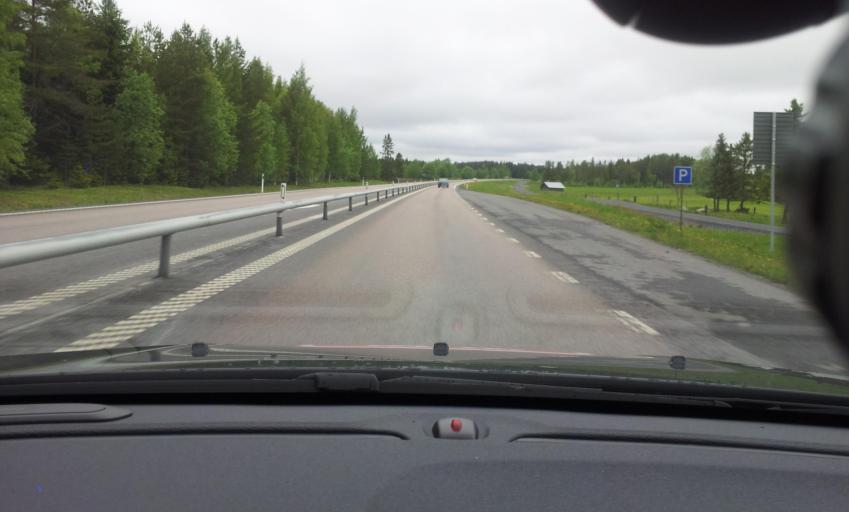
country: SE
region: Jaemtland
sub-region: OEstersunds Kommun
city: Ostersund
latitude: 63.2570
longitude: 14.5583
